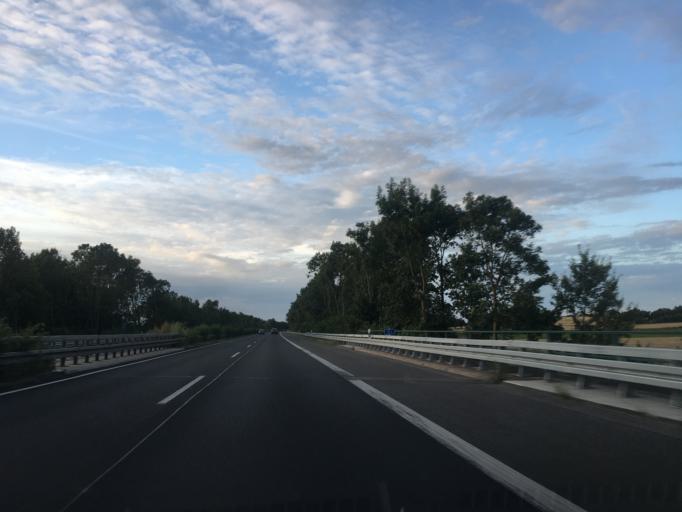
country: DE
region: North Rhine-Westphalia
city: Julich
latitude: 50.9398
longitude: 6.3434
